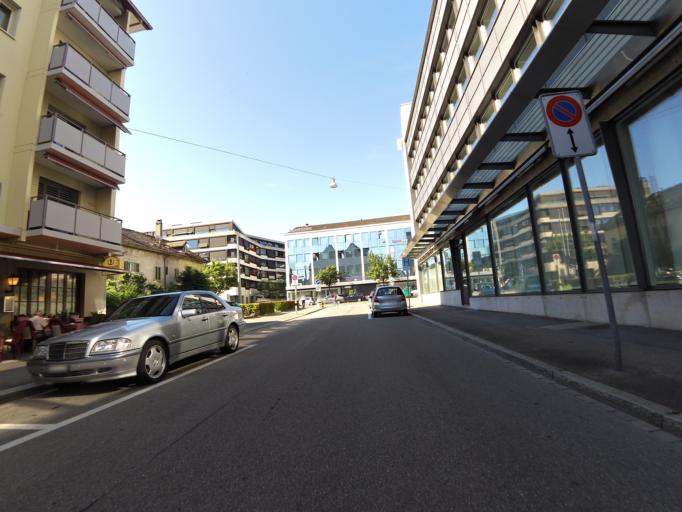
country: CH
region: Zurich
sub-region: Bezirk Zuerich
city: Zuerich (Kreis 9) / Altstetten
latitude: 47.3887
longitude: 8.4847
